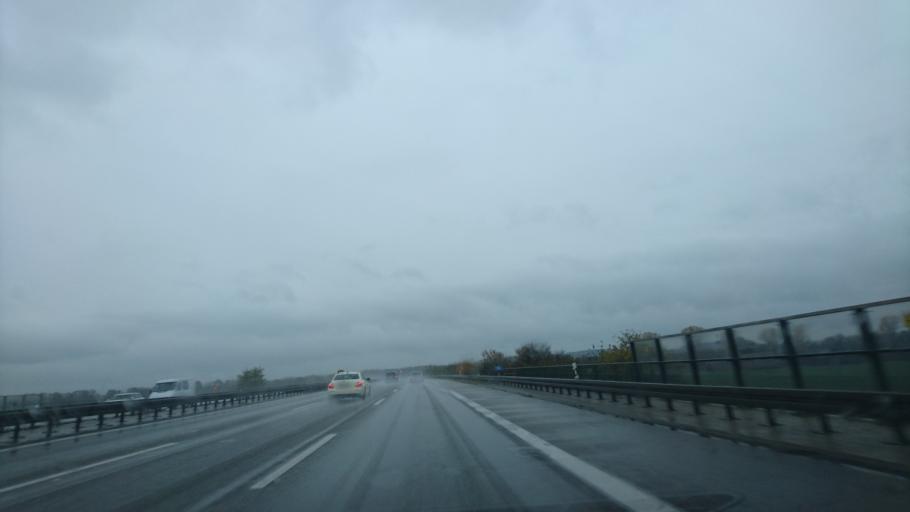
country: DE
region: Bavaria
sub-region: Upper Bavaria
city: Neufahrn bei Freising
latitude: 48.3328
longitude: 11.6750
